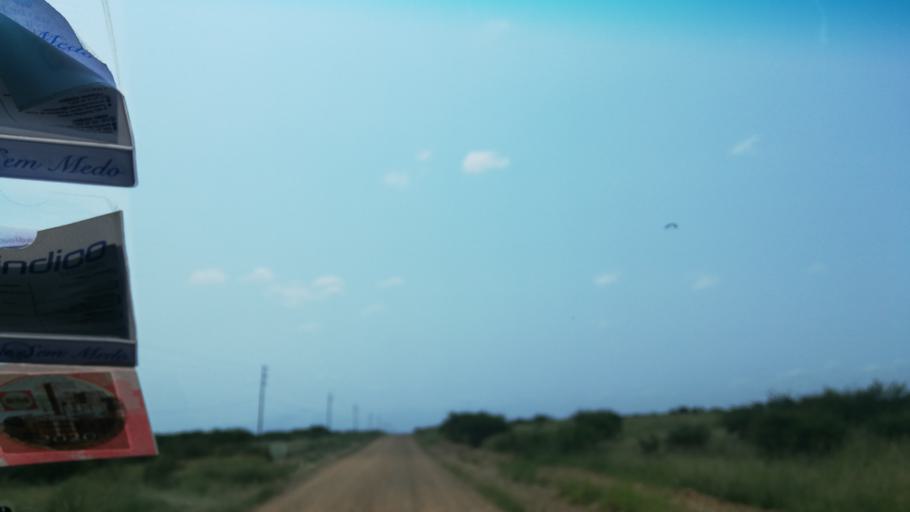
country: MZ
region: Maputo
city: Matola
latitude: -26.0761
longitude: 32.3909
